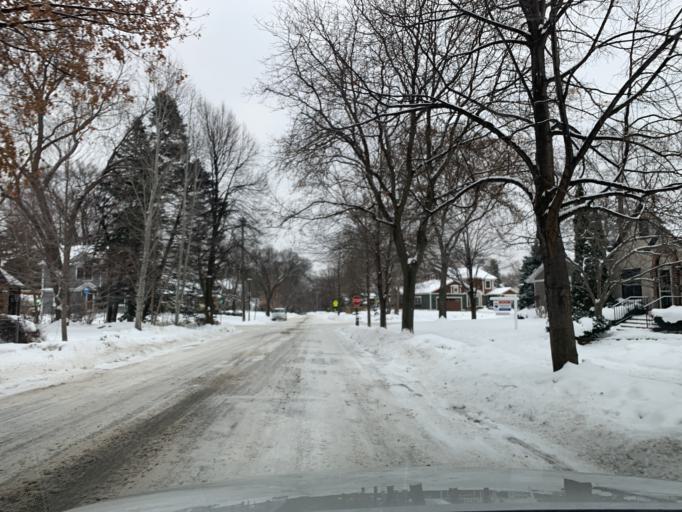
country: US
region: Minnesota
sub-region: Hennepin County
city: Saint Louis Park
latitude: 44.9311
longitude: -93.3393
